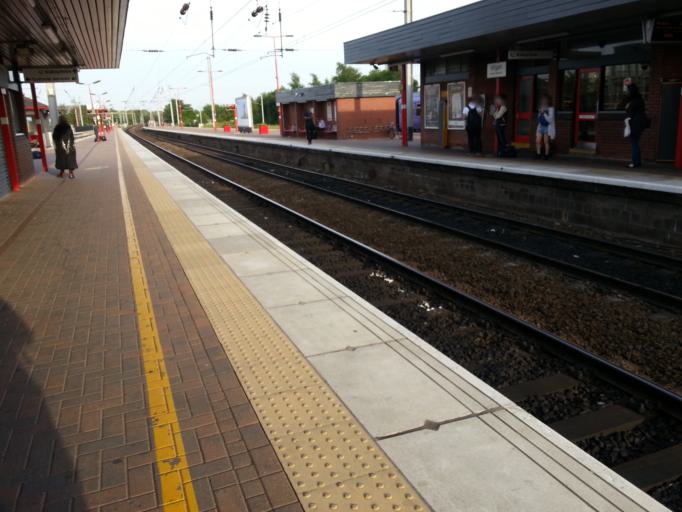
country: GB
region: England
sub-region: Borough of Wigan
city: Ince-in-Makerfield
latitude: 53.5434
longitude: -2.6331
